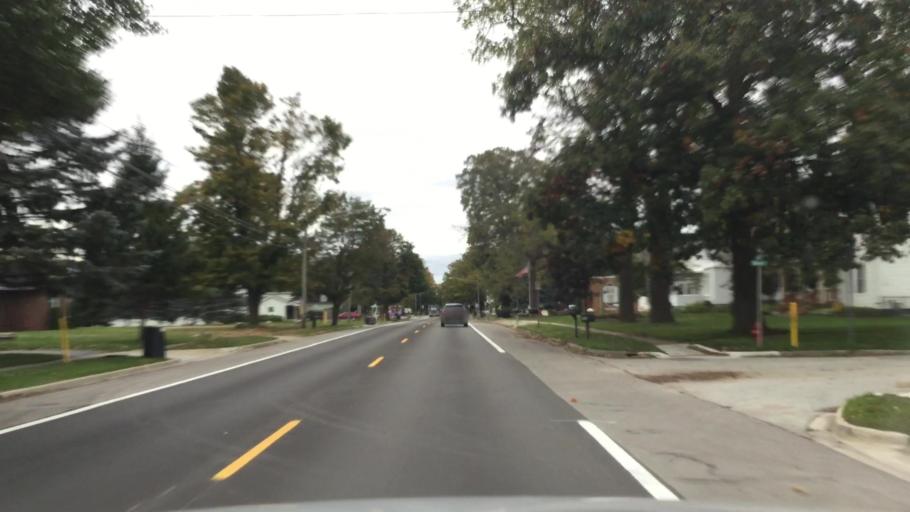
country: US
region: Michigan
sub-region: Macomb County
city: Memphis
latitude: 42.8939
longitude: -82.7689
